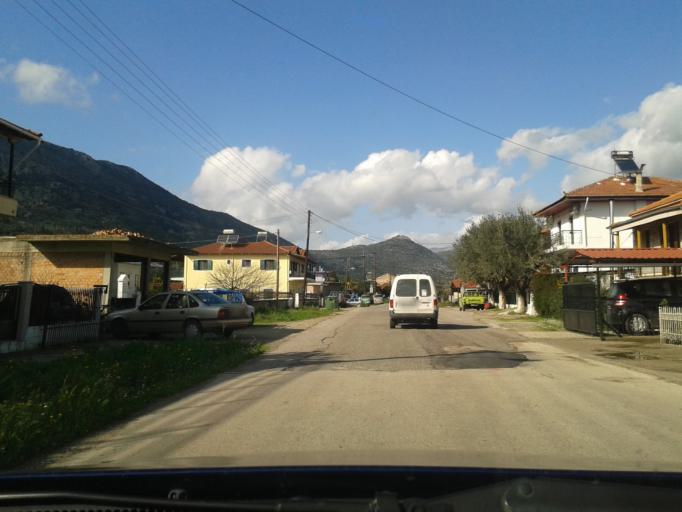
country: GR
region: West Greece
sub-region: Nomos Aitolias kai Akarnanias
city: Astakos
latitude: 38.5762
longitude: 21.0917
